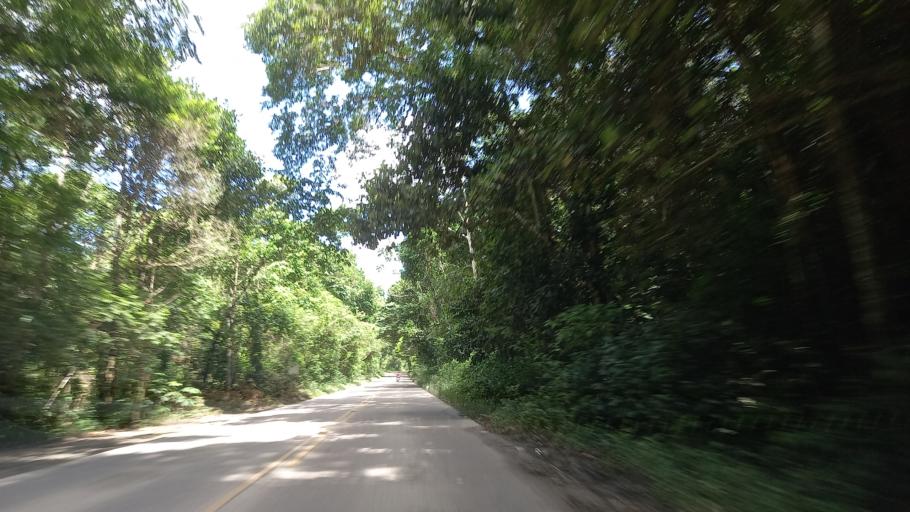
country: BR
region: Pernambuco
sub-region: Rio Formoso
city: Rio Formoso
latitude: -8.7257
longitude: -35.1730
